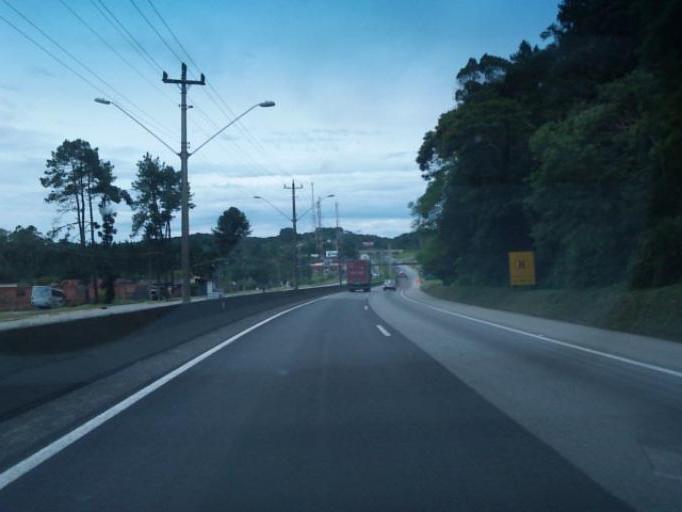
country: BR
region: Sao Paulo
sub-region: Juquitiba
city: Juquitiba
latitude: -23.9189
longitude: -46.9903
